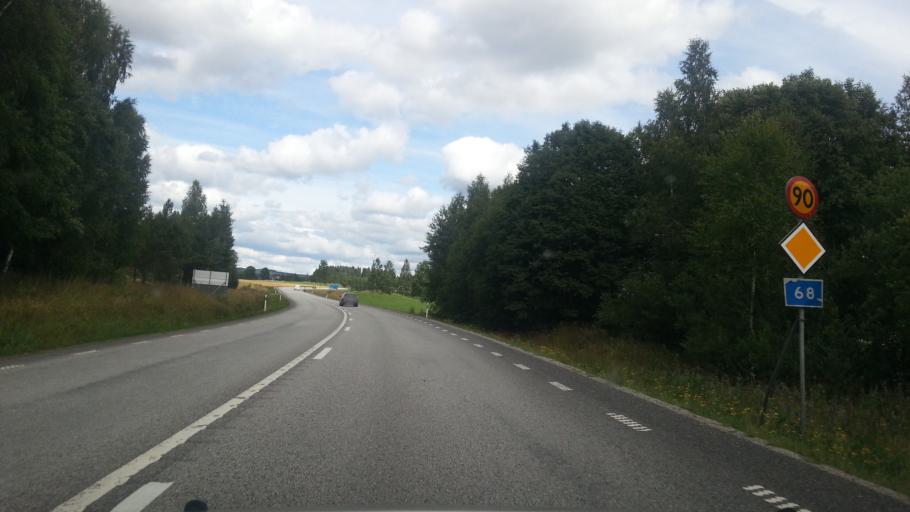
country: SE
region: OErebro
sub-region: Lindesbergs Kommun
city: Lindesberg
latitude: 59.6287
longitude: 15.2157
